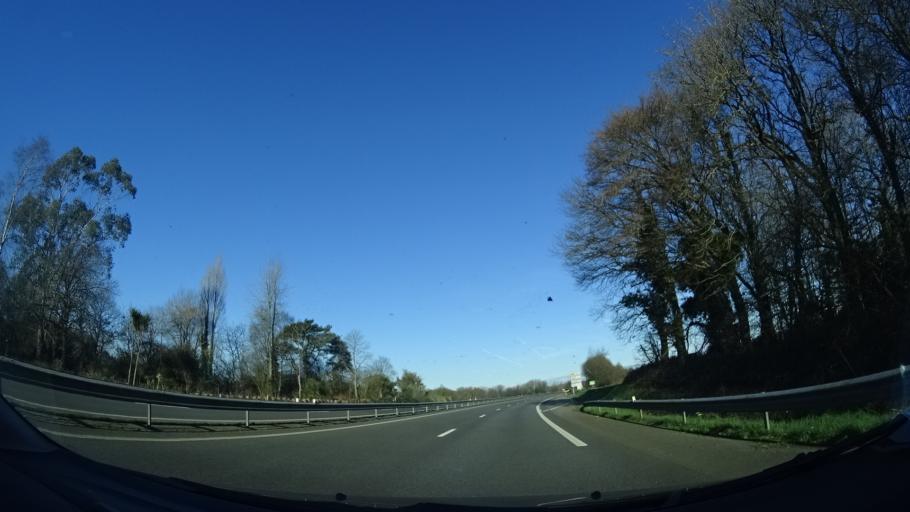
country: FR
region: Brittany
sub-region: Departement du Finistere
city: Taule
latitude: 48.5958
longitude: -3.8887
